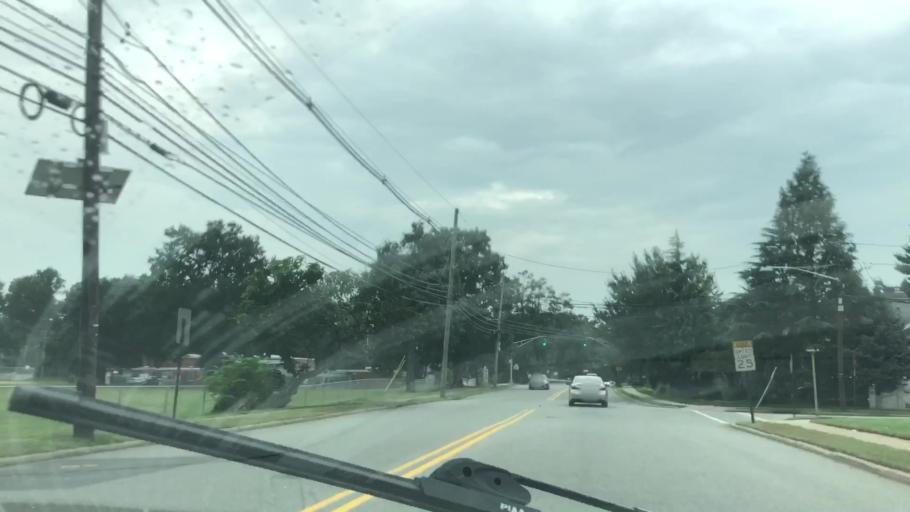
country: US
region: New Jersey
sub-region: Essex County
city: Upper Montclair
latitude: 40.8606
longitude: -74.1873
